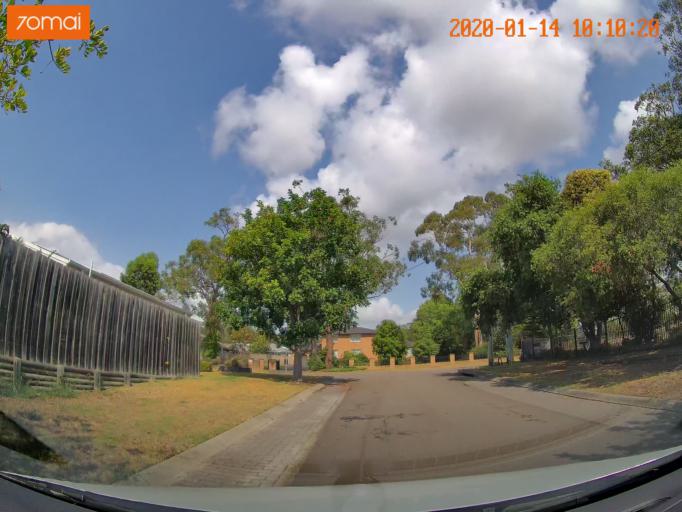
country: AU
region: New South Wales
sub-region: Wyong Shire
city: Kingfisher Shores
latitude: -33.1226
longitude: 151.5361
